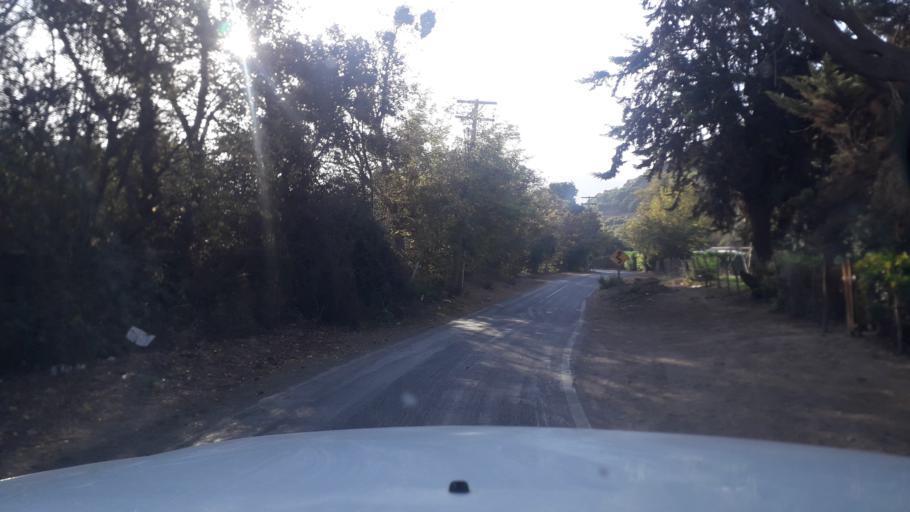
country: CL
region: Valparaiso
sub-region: Provincia de San Felipe
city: Llaillay
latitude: -32.8196
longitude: -71.0273
